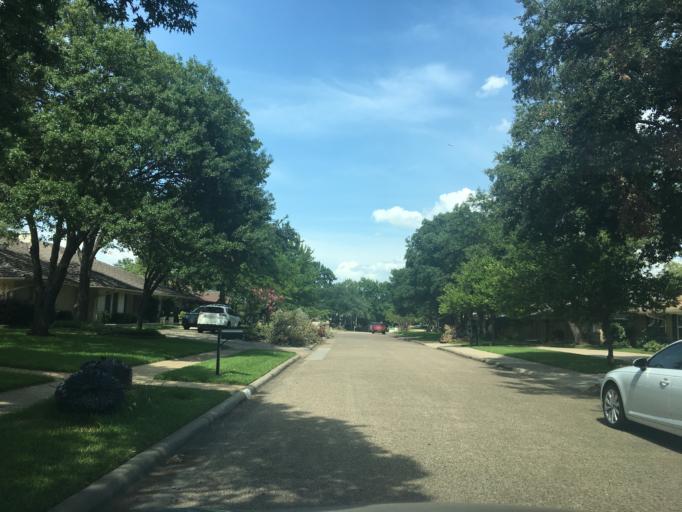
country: US
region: Texas
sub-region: Dallas County
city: Addison
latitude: 32.9211
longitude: -96.8361
